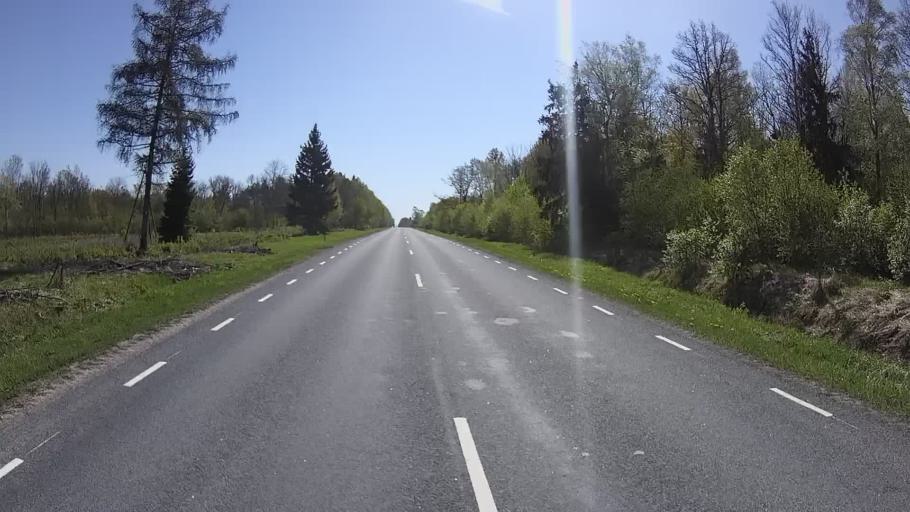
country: EE
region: Laeaene
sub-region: Lihula vald
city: Lihula
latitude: 58.5490
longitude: 23.9910
